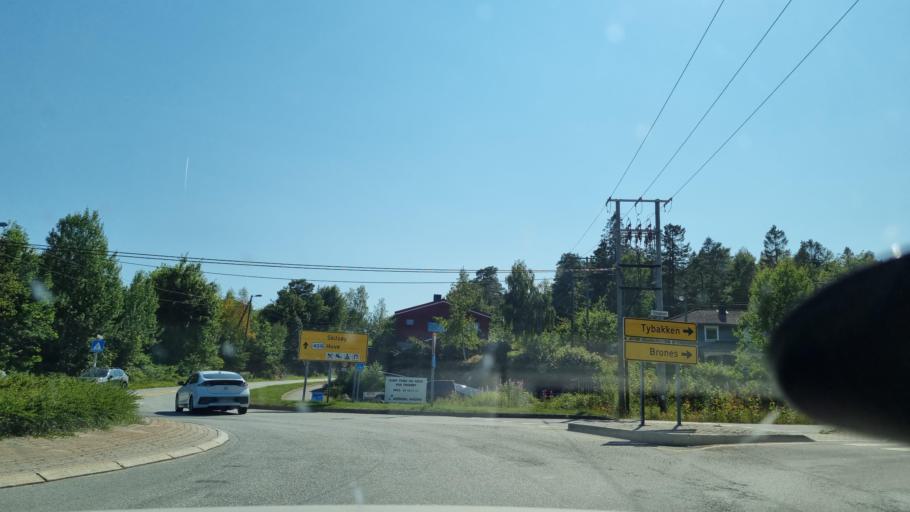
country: NO
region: Aust-Agder
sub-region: Arendal
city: Arendal
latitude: 58.4670
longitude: 8.8247
